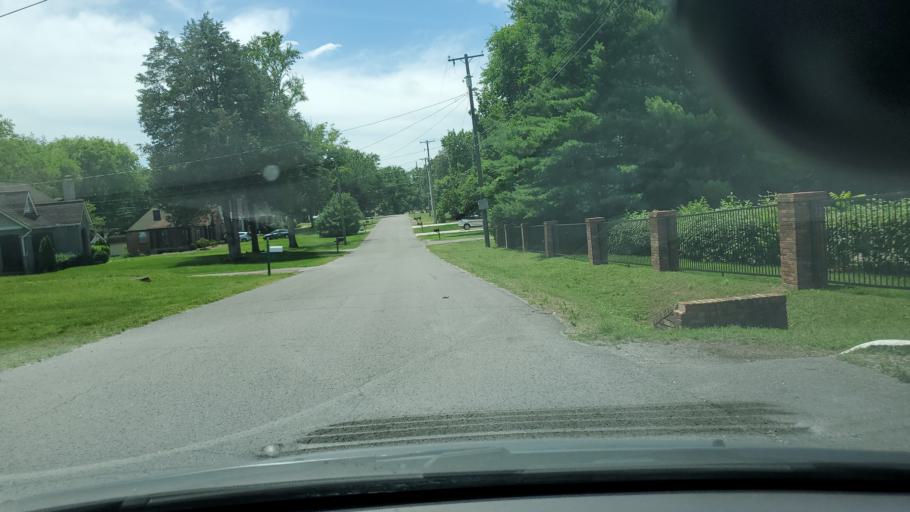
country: US
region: Tennessee
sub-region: Davidson County
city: Nashville
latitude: 36.2256
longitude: -86.7270
